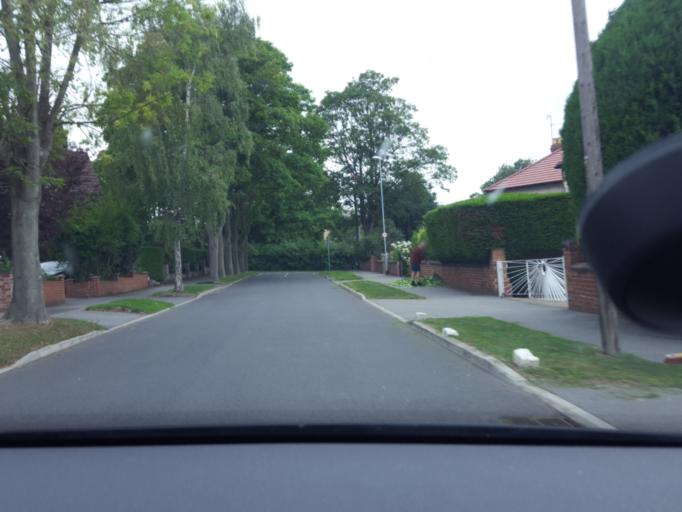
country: GB
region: England
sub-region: City and Borough of Leeds
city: Gildersome
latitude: 53.8015
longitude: -1.6065
